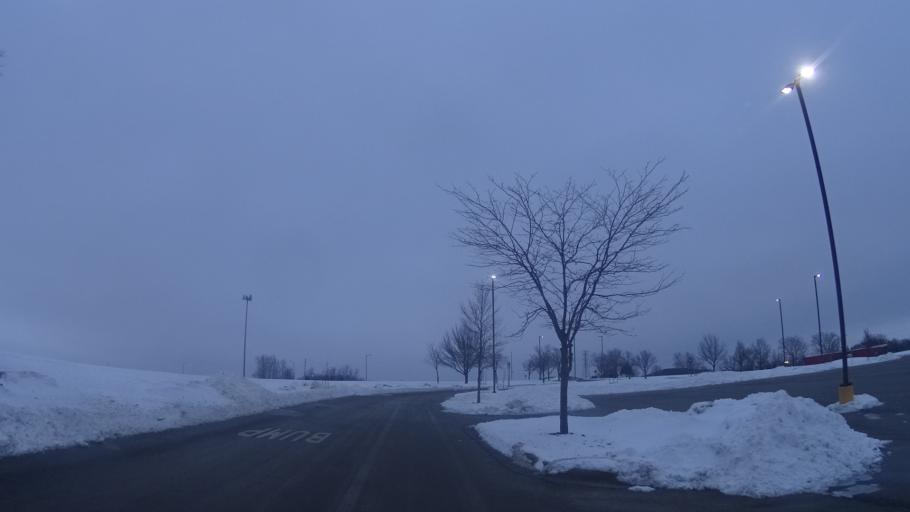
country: US
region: Nebraska
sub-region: Sarpy County
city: Offutt Air Force Base
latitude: 41.1522
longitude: -95.9226
